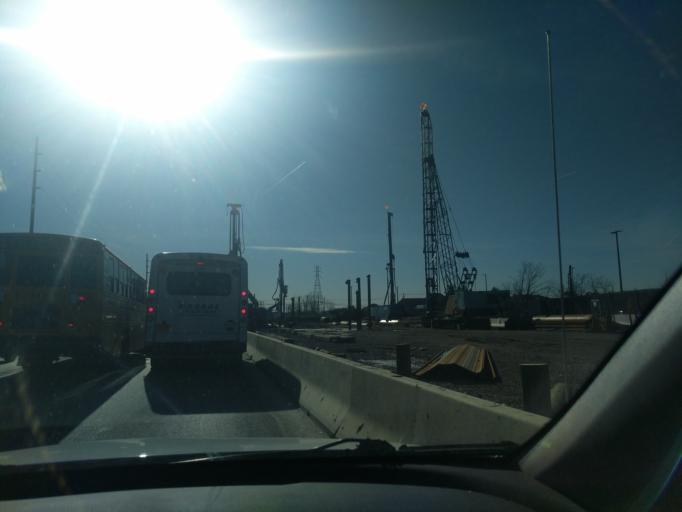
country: US
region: New York
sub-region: Nassau County
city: Inwood
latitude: 40.6296
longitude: -73.7388
